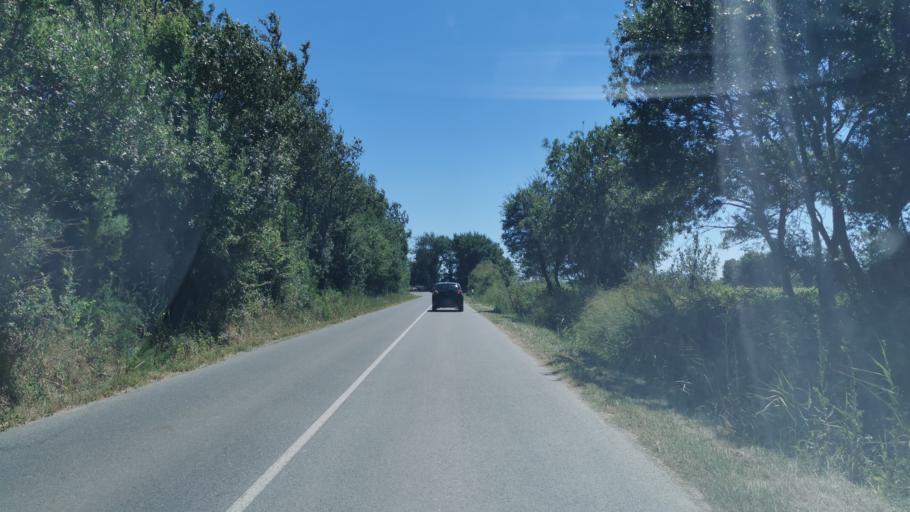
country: FR
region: Languedoc-Roussillon
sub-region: Departement de l'Aude
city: Vinassan
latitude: 43.2196
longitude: 3.0756
